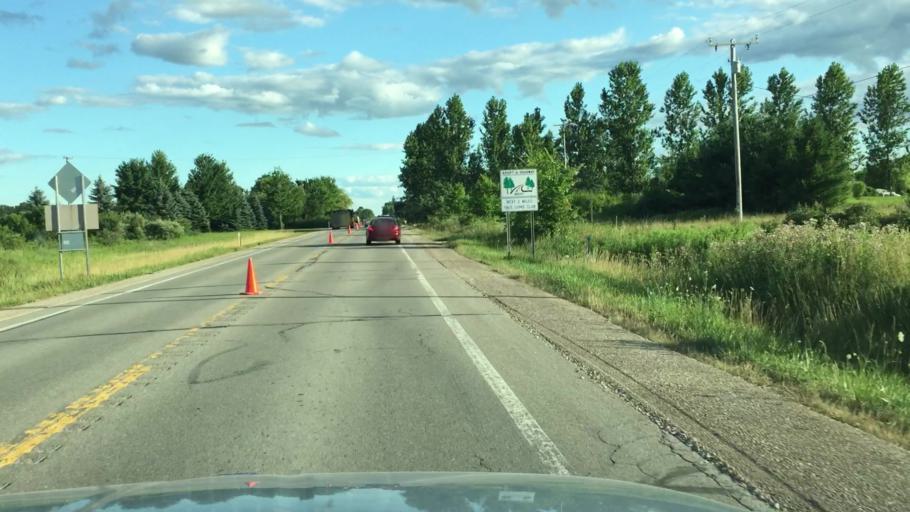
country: US
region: Michigan
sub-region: Saint Clair County
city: Yale
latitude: 43.1002
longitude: -82.7668
